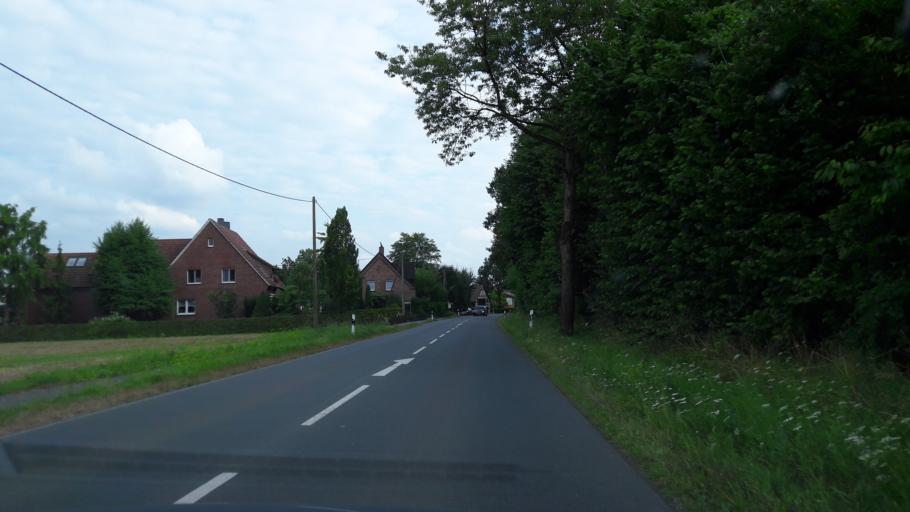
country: DE
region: North Rhine-Westphalia
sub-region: Regierungsbezirk Munster
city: Ennigerloh
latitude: 51.8195
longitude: 7.9533
